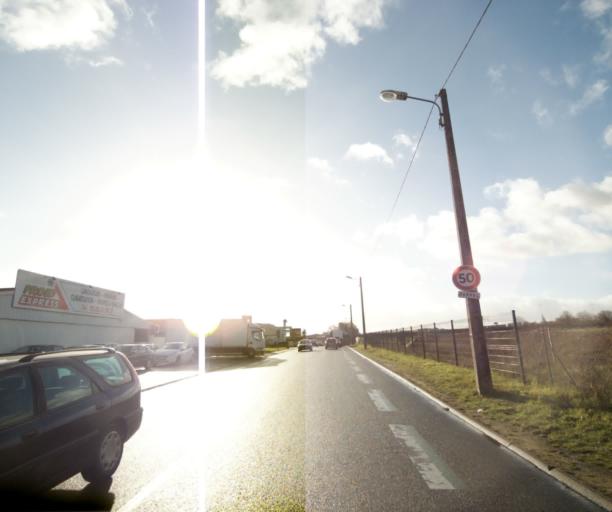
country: FR
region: Pays de la Loire
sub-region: Departement de la Sarthe
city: La Chapelle-Saint-Aubin
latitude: 48.0294
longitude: 0.1720
